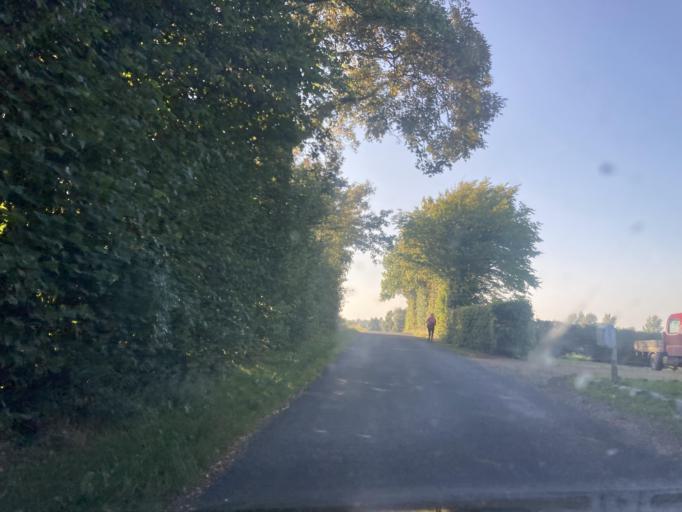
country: DK
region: South Denmark
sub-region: Svendborg Kommune
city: Thuro By
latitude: 55.1128
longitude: 10.7377
